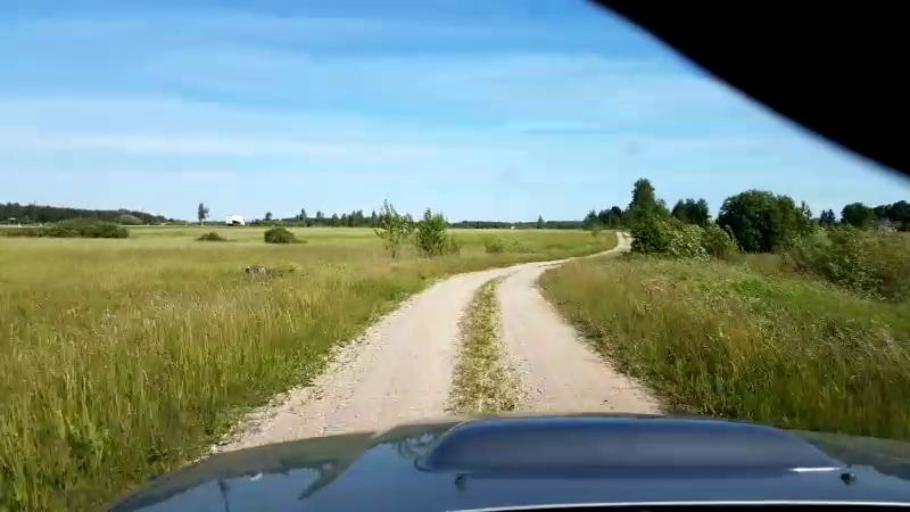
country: EE
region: Paernumaa
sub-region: Sauga vald
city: Sauga
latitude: 58.4847
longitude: 24.5305
